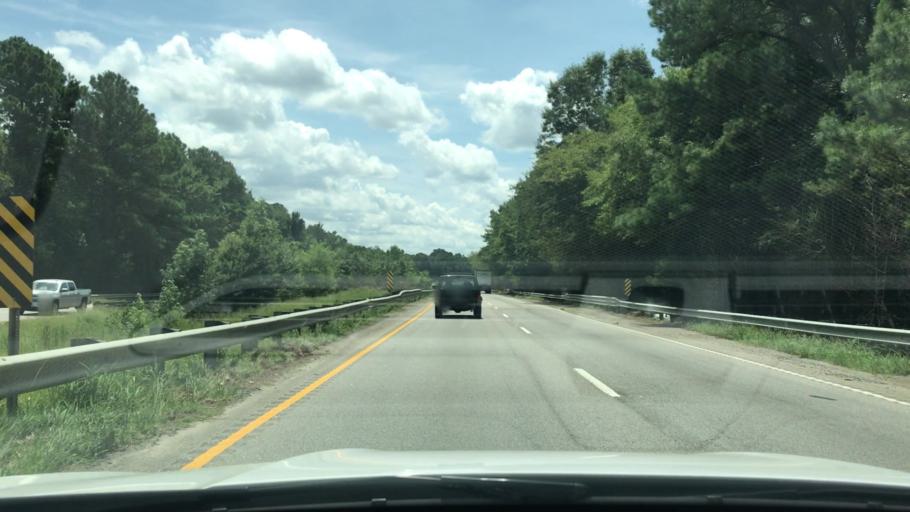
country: US
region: South Carolina
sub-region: Berkeley County
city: Goose Creek
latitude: 33.0510
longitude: -80.0341
